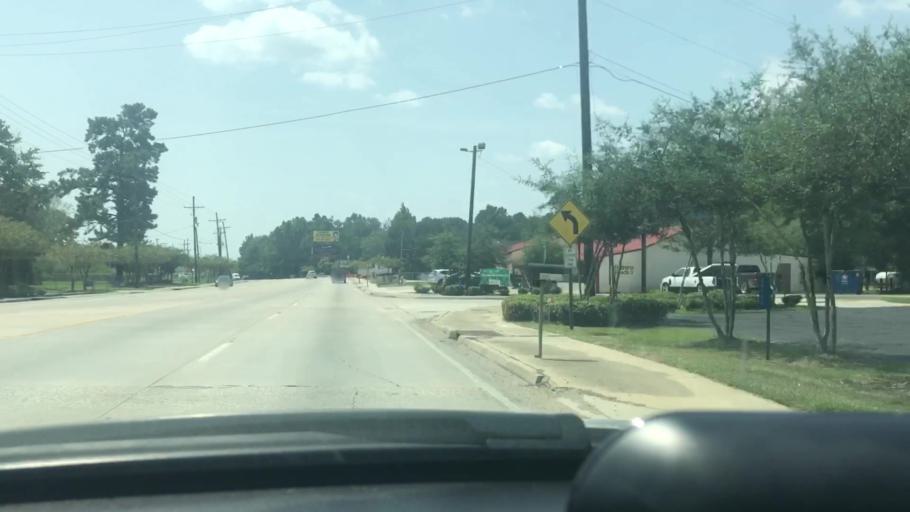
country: US
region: Louisiana
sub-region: Livingston Parish
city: Walker
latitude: 30.4853
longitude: -90.8626
